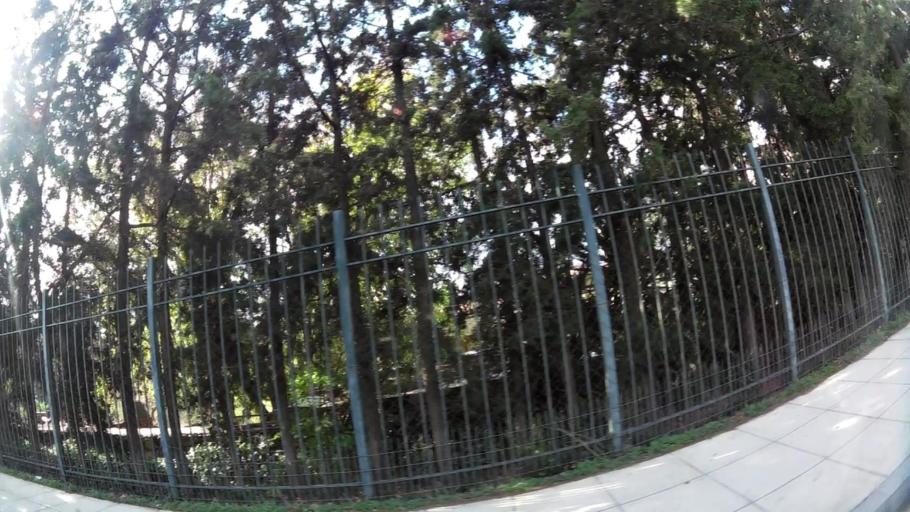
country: GR
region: Attica
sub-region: Nomarchia Athinas
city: Melissia
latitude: 38.0575
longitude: 23.8202
